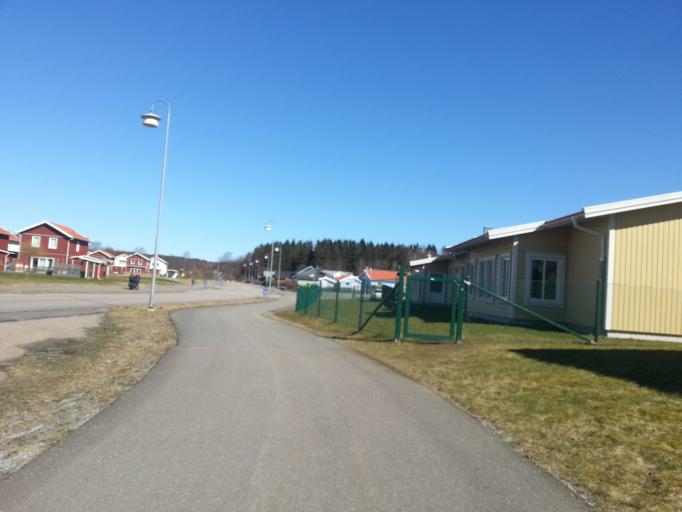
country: SE
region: Vaestra Goetaland
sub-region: Kungalvs Kommun
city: Kungalv
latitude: 57.8944
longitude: 11.9510
